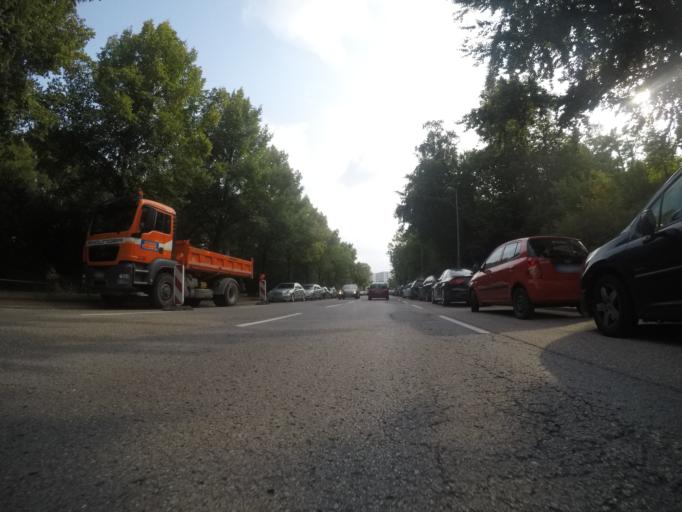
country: DE
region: Baden-Wuerttemberg
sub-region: Regierungsbezirk Stuttgart
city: Stuttgart Feuerbach
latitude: 48.8042
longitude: 9.1744
